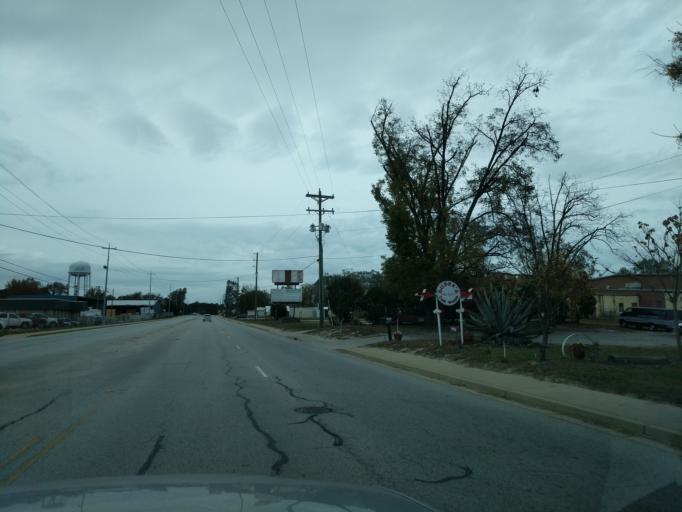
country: US
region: South Carolina
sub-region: Newberry County
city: Newberry
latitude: 34.3018
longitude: -81.6200
